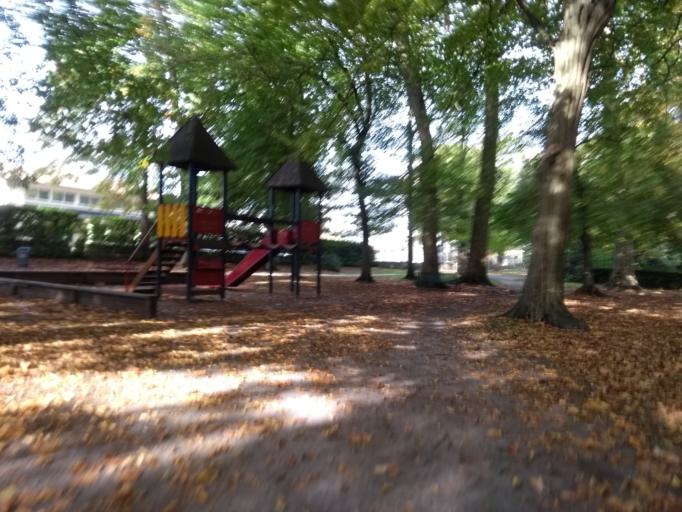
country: FR
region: Aquitaine
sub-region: Departement de la Gironde
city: Pessac
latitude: 44.7977
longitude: -0.6427
